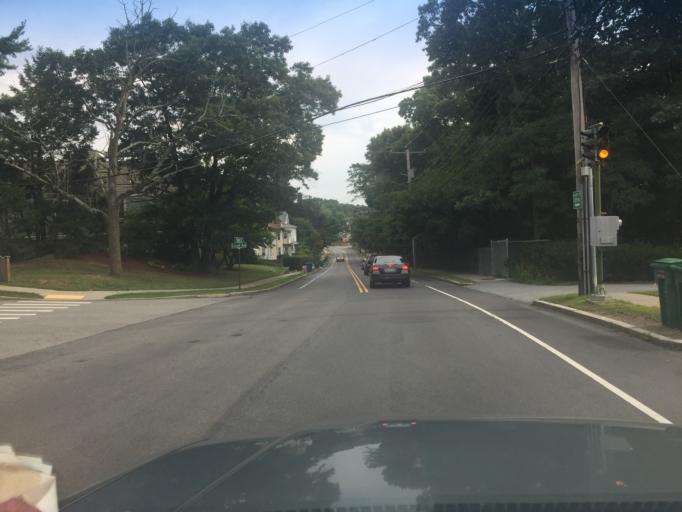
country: US
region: Massachusetts
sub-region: Middlesex County
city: Newton
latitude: 42.3144
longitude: -71.2156
